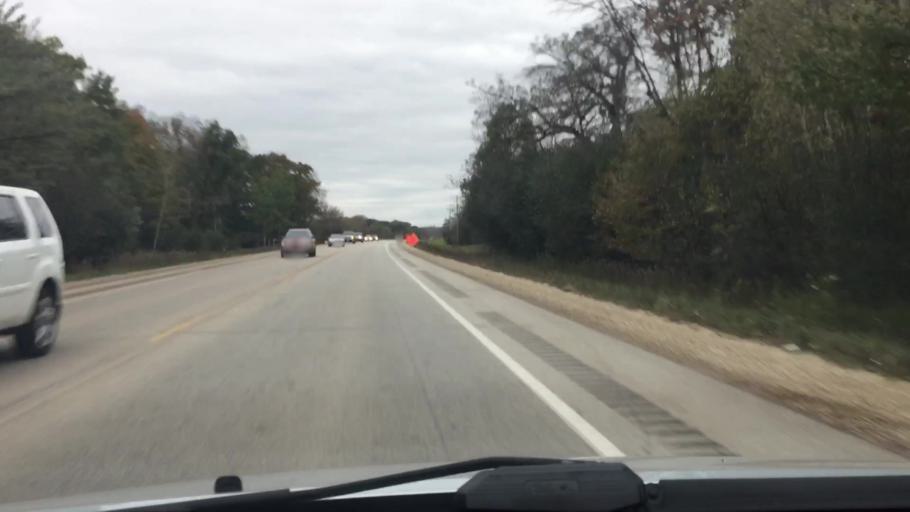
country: US
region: Wisconsin
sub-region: Waukesha County
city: Wales
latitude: 42.9678
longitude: -88.3140
